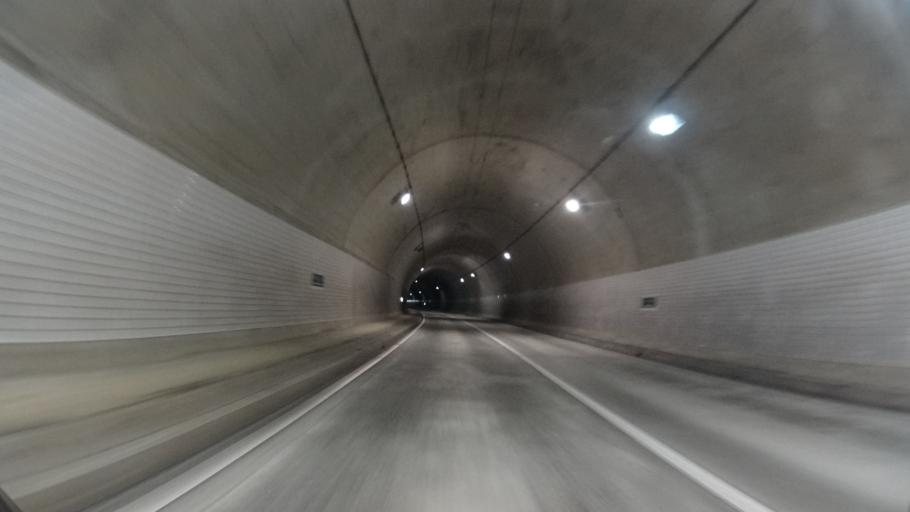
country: JP
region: Ehime
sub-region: Nishiuwa-gun
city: Ikata-cho
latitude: 33.4519
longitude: 132.2725
